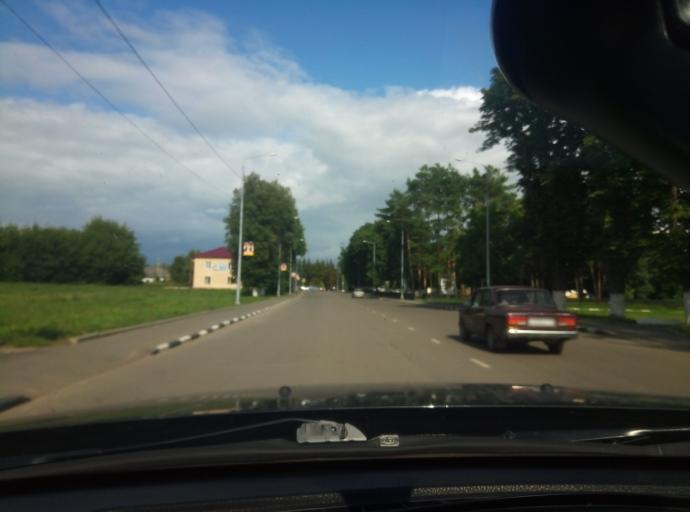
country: RU
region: Tula
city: Donskoy
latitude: 53.9676
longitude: 38.3347
